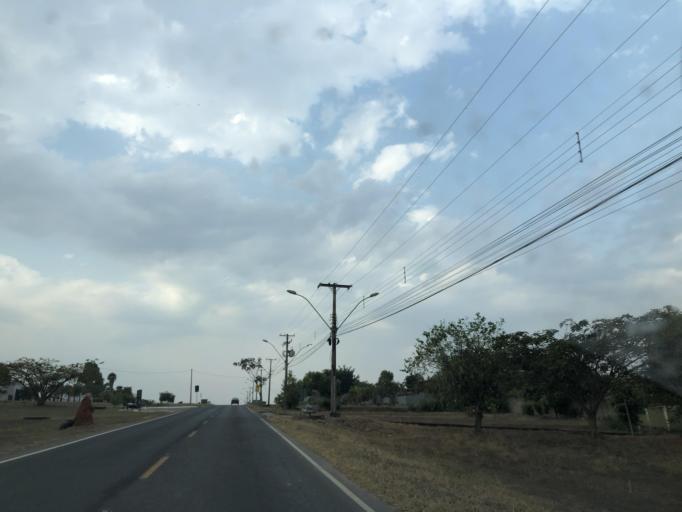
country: BR
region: Federal District
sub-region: Brasilia
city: Brasilia
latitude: -15.9337
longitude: -47.9737
